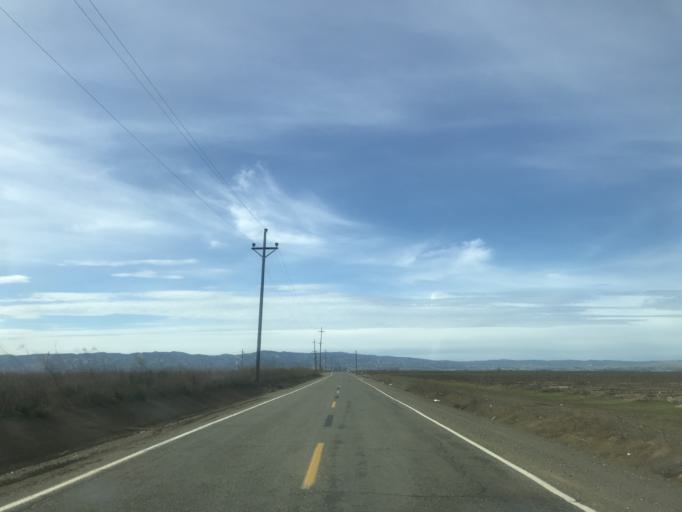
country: US
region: California
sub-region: Yolo County
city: Cottonwood
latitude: 38.6637
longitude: -121.9010
